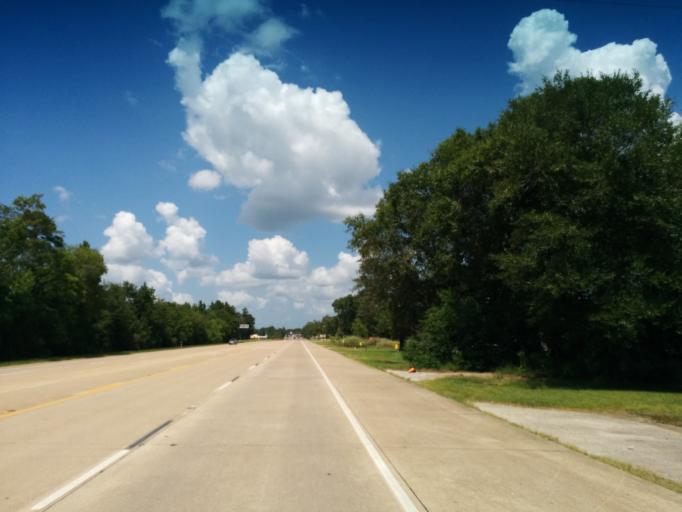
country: US
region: Texas
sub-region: Jasper County
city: Buna
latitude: 30.4330
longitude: -93.9765
